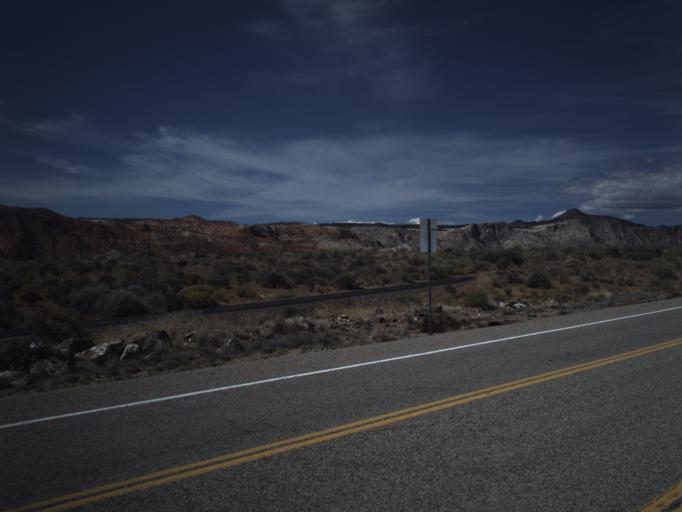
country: US
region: Utah
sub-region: Washington County
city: Ivins
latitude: 37.2094
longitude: -113.6295
